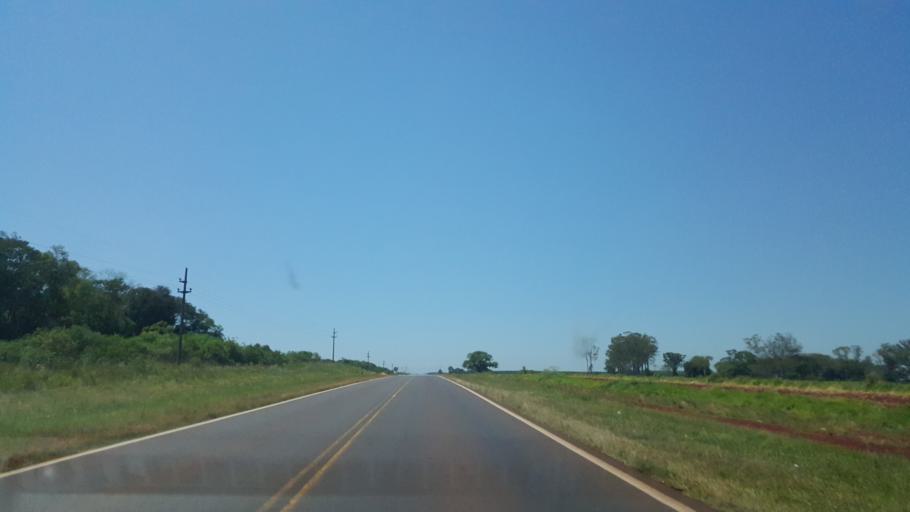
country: AR
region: Corrientes
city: Santo Tome
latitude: -28.3656
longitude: -56.1110
